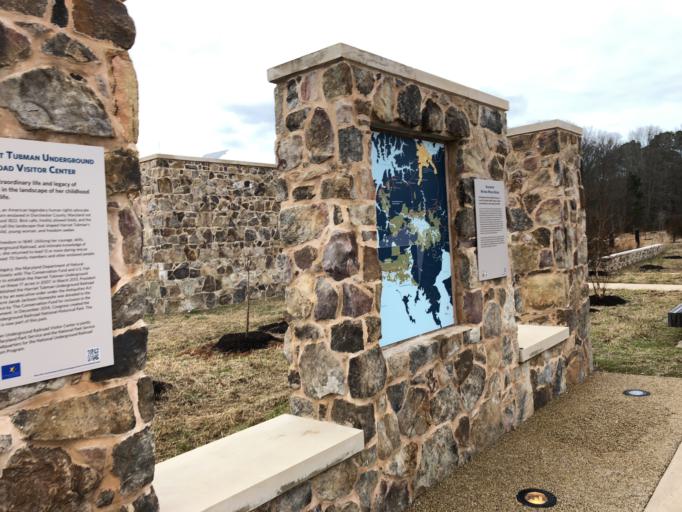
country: US
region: Maryland
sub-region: Dorchester County
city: Cambridge
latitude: 38.4494
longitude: -76.1382
